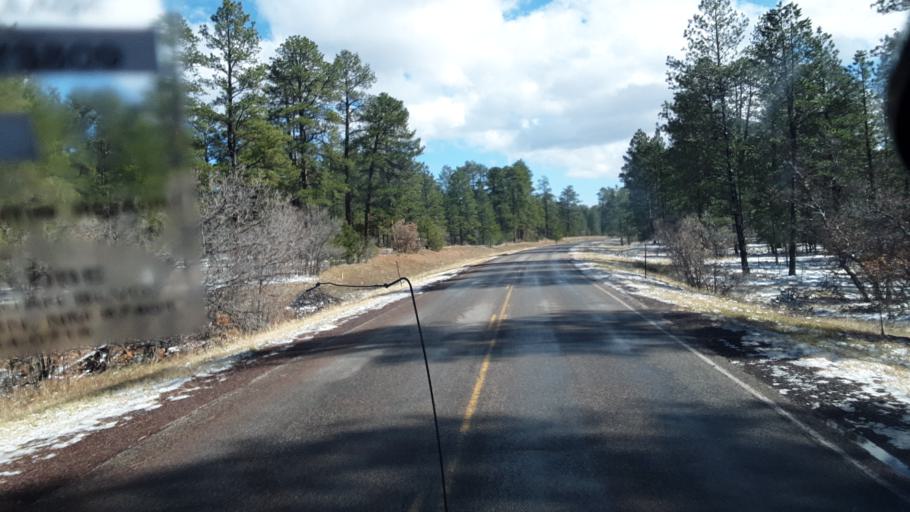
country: US
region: New Mexico
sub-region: Rio Arriba County
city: Santa Teresa
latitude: 36.2002
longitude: -106.7645
